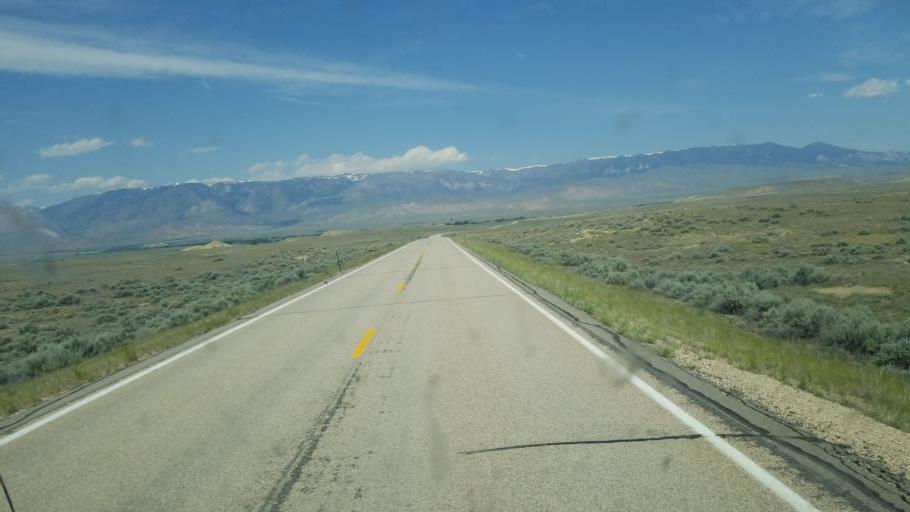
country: US
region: Montana
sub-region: Carbon County
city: Red Lodge
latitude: 44.8894
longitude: -109.0789
